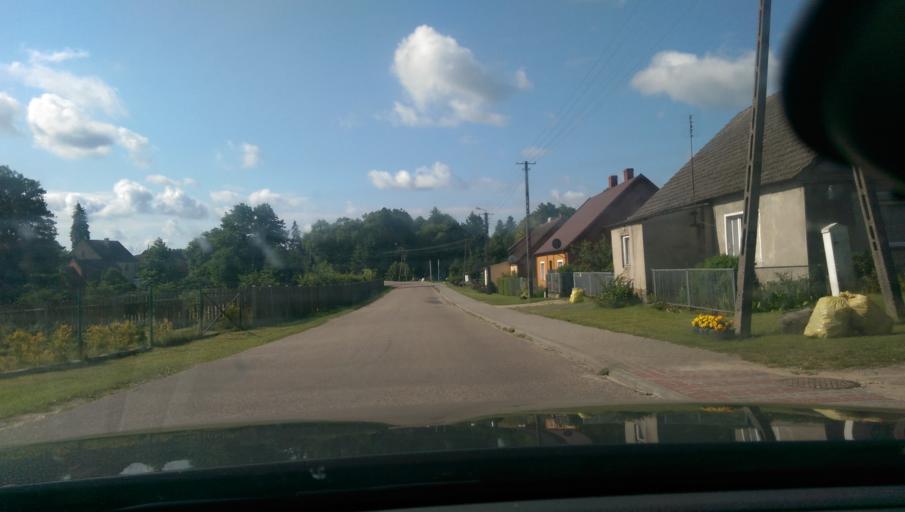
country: PL
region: West Pomeranian Voivodeship
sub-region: Powiat walecki
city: Walcz
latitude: 53.3469
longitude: 16.5700
